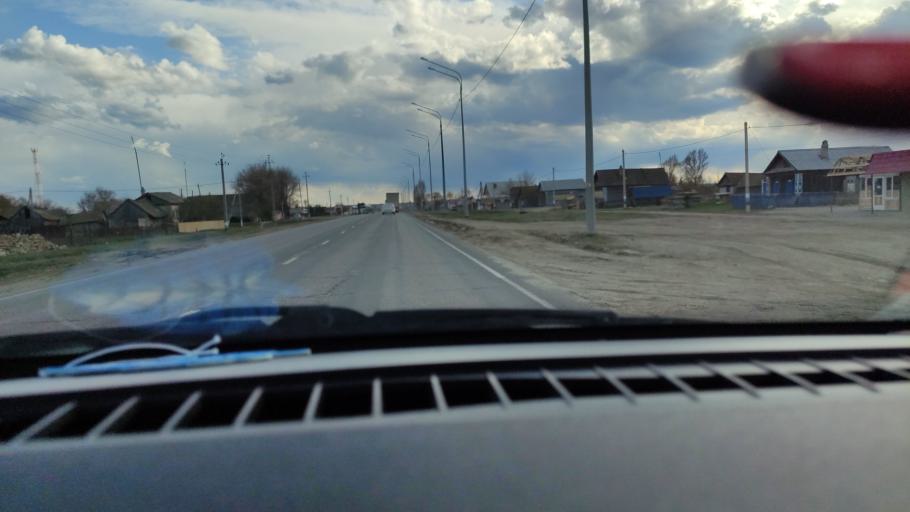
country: RU
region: Saratov
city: Sinodskoye
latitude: 51.9850
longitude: 46.6626
